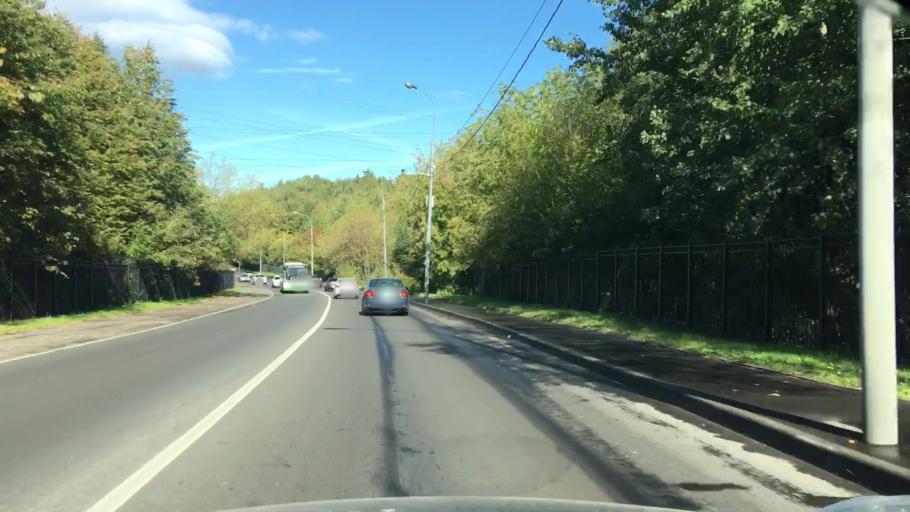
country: RU
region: Moskovskaya
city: Izmaylovo
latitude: 55.7829
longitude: 37.8209
